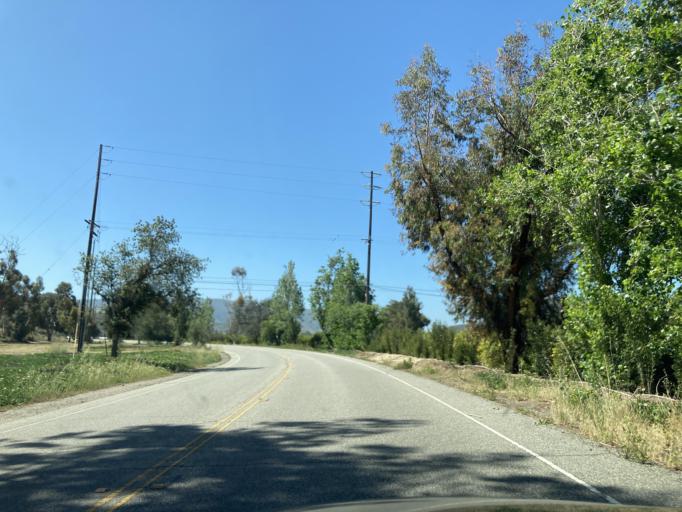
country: US
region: California
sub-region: Ventura County
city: Camarillo
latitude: 34.1763
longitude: -119.0434
